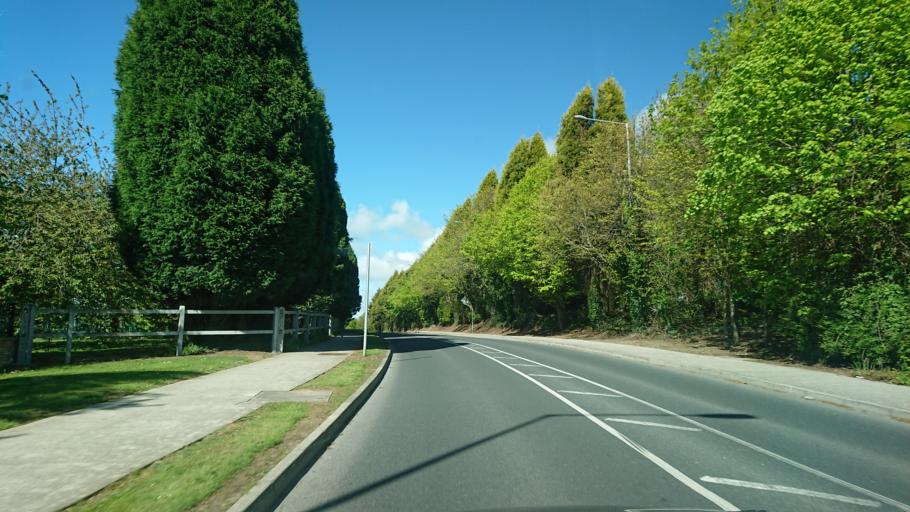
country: IE
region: Munster
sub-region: Waterford
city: Waterford
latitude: 52.2540
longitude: -7.1494
